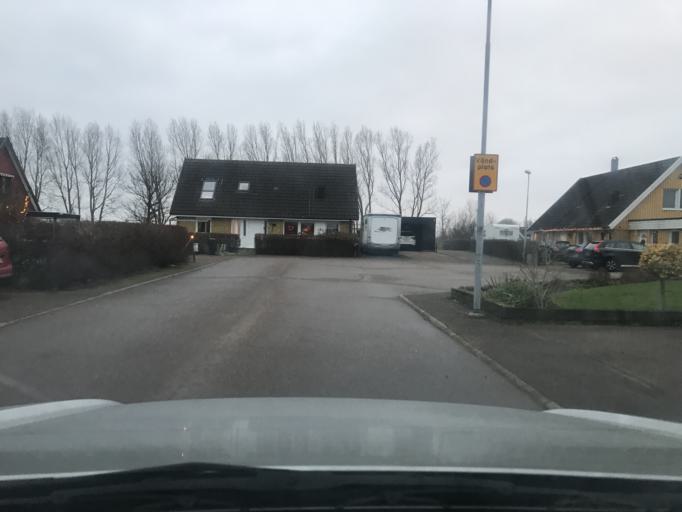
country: SE
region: Skane
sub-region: Hoganas Kommun
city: Hoganas
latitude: 56.2384
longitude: 12.5482
